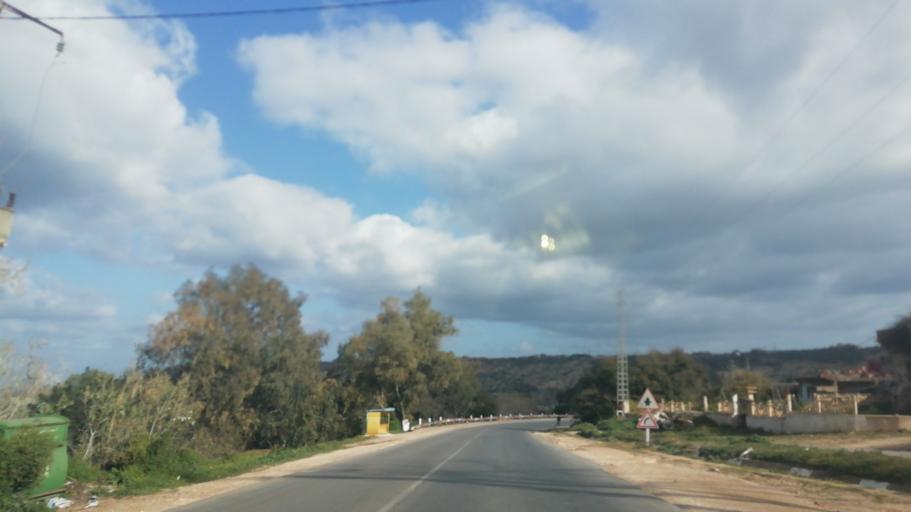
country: DZ
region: Relizane
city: Mazouna
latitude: 36.2981
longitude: 0.6579
